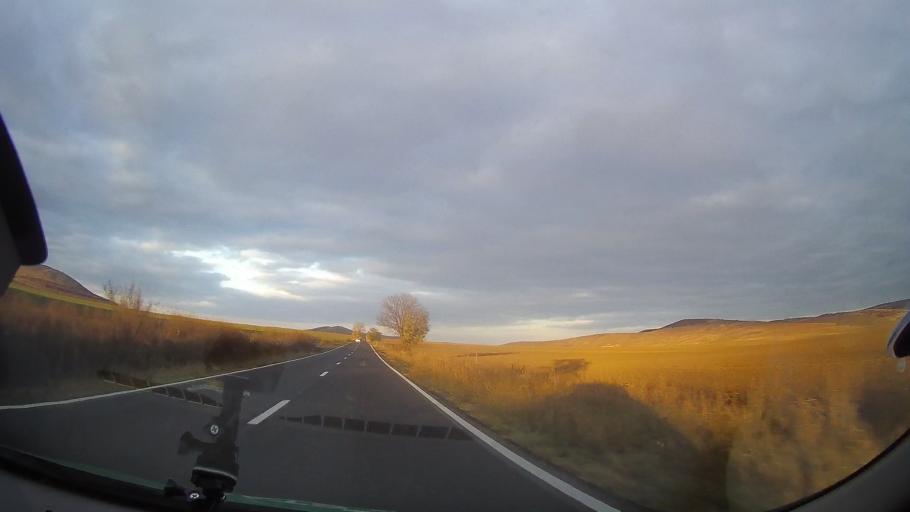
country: RO
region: Tulcea
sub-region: Comuna Nalbant
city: Nicolae Balcescu
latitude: 44.9736
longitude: 28.5422
